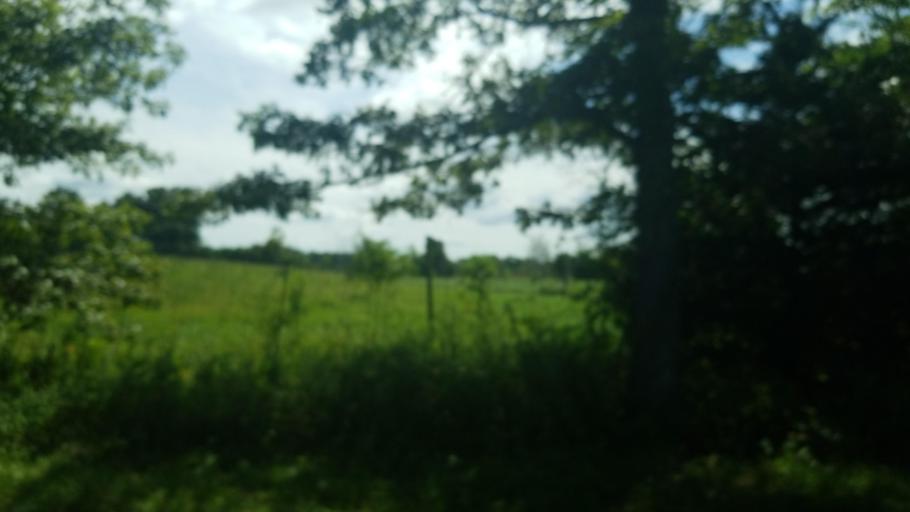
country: US
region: Illinois
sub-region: Saline County
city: Carrier Mills
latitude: 37.7918
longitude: -88.7602
